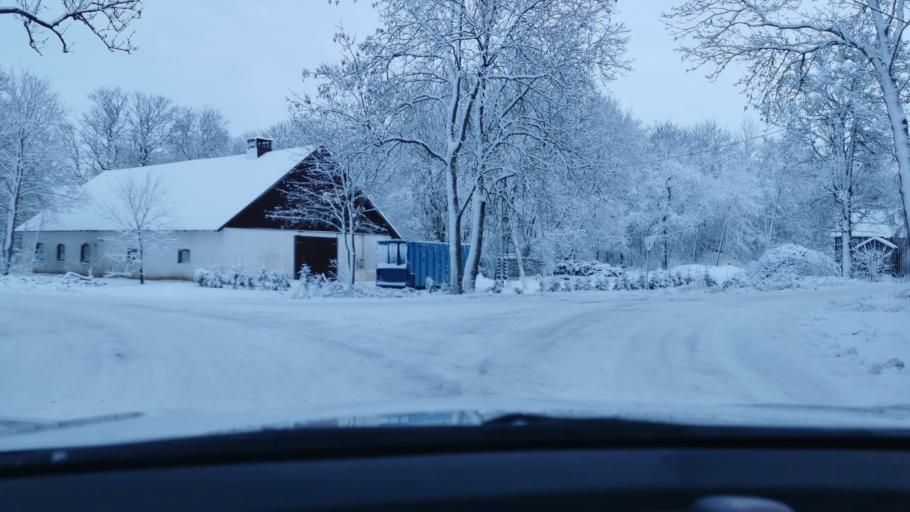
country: EE
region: Laeaene-Virumaa
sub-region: Haljala vald
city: Haljala
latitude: 59.4698
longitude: 26.3403
